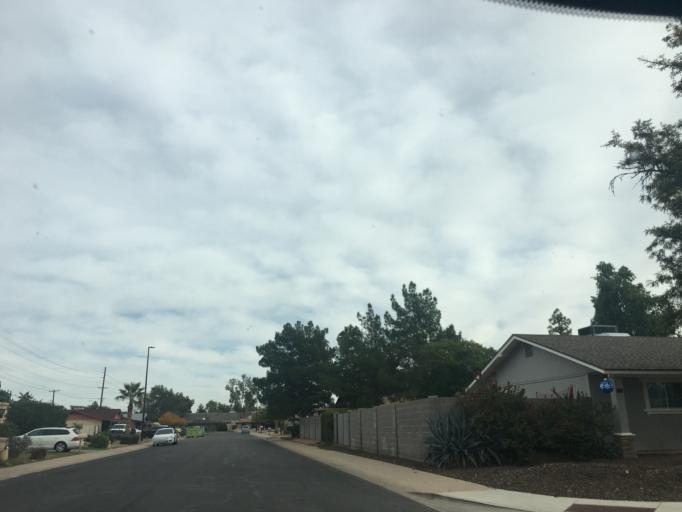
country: US
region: Arizona
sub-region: Maricopa County
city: Gilbert
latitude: 33.3640
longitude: -111.7963
